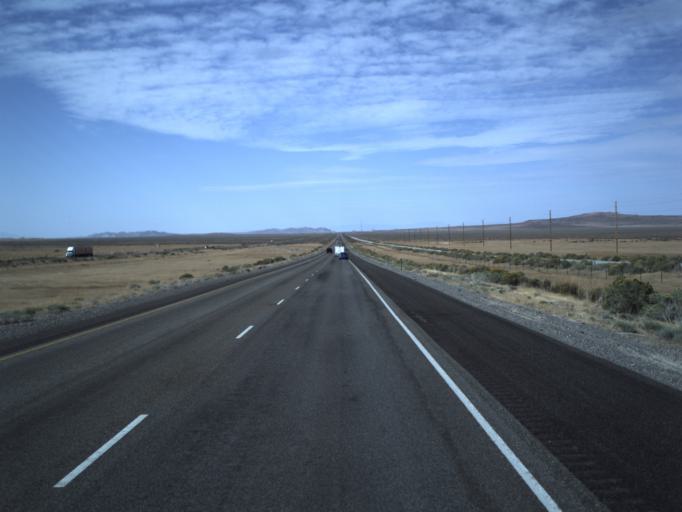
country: US
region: Utah
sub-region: Tooele County
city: Grantsville
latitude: 40.7539
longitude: -113.0359
